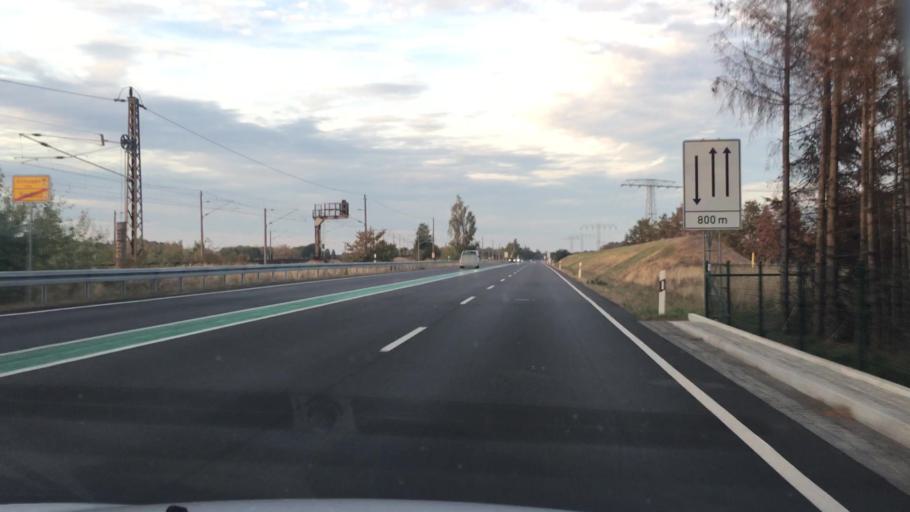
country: DE
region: Brandenburg
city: Grossraschen
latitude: 51.5556
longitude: 14.0585
